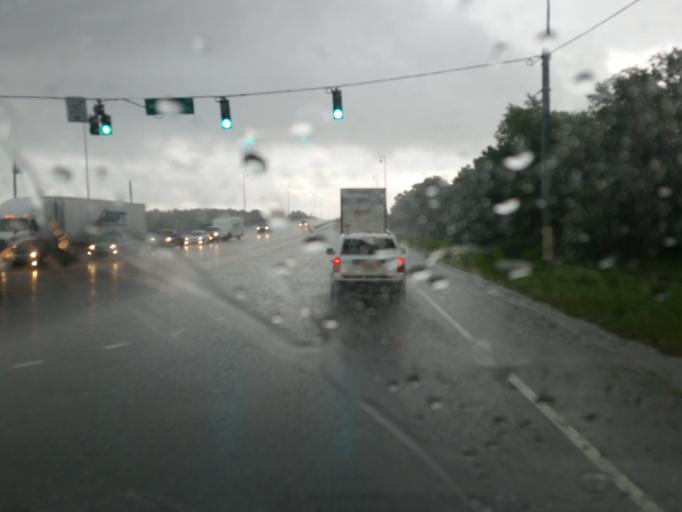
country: US
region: Alabama
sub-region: Mobile County
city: Prichard
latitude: 30.7303
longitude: -88.0669
